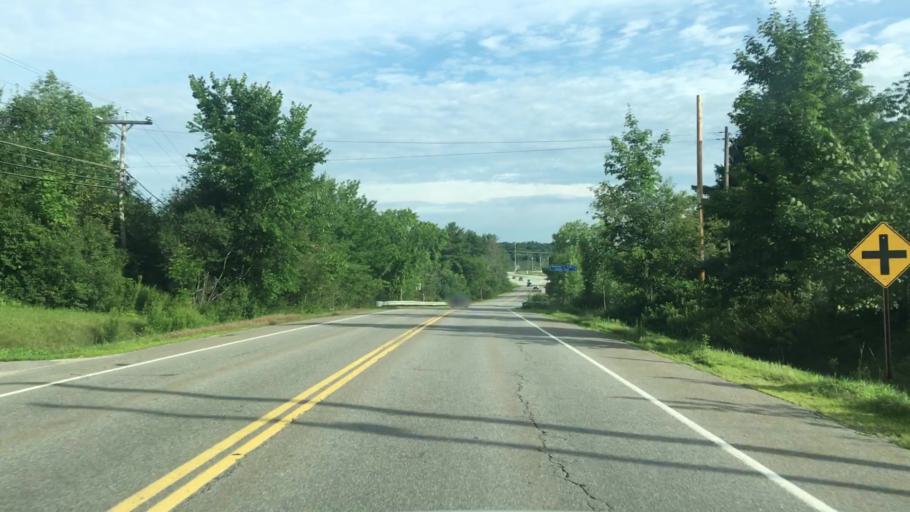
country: US
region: Maine
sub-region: Cumberland County
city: Gorham
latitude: 43.6473
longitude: -70.4239
